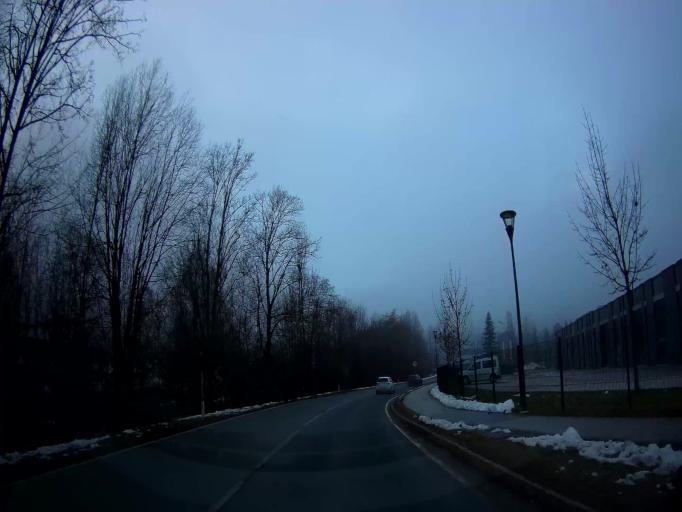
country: AT
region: Salzburg
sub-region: Politischer Bezirk Zell am See
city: Kaprun
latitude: 47.2622
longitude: 12.7449
